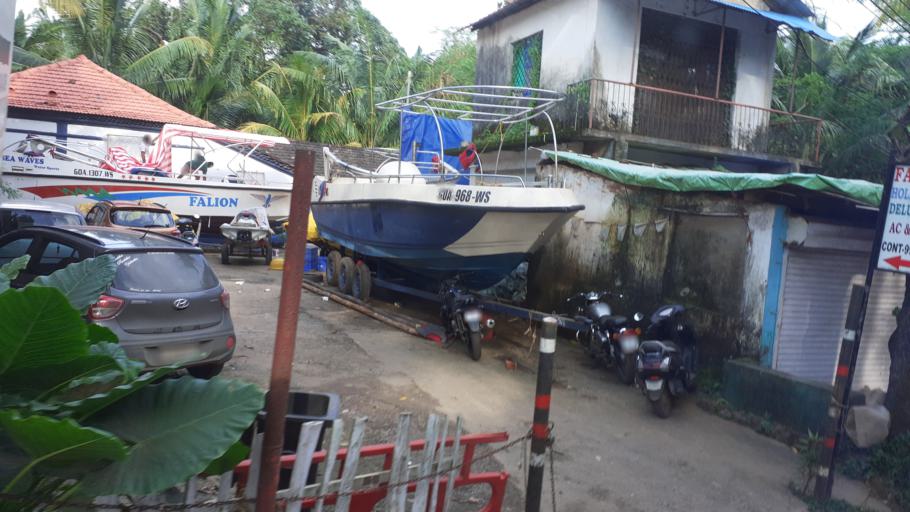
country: IN
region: Goa
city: Calangute
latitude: 15.5538
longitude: 73.7575
